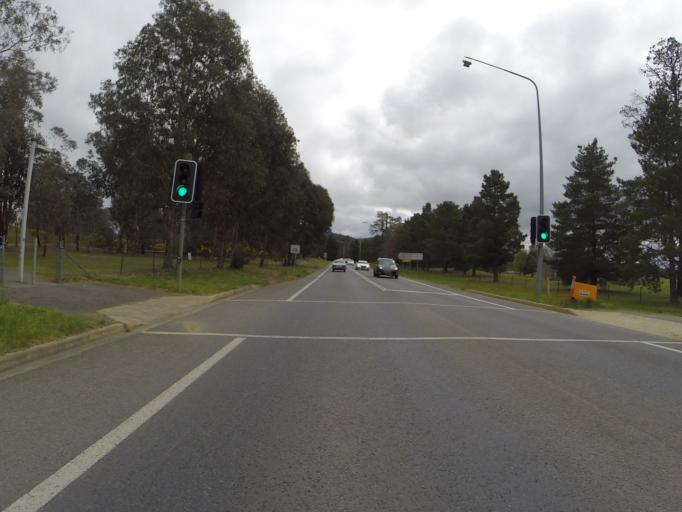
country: AU
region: Australian Capital Territory
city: Canberra
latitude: -35.2920
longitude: 149.1702
